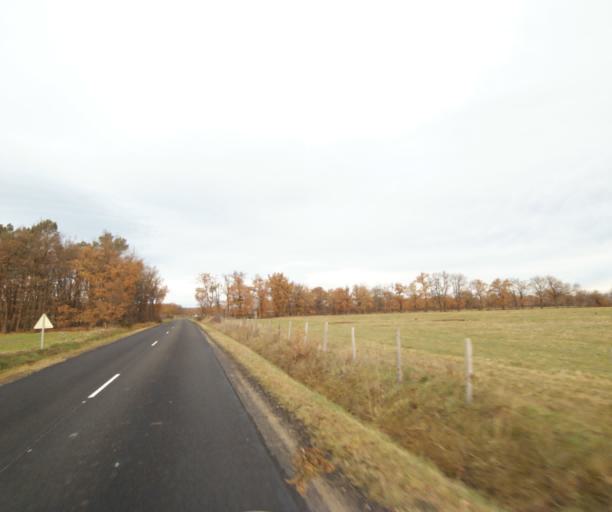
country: FR
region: Rhone-Alpes
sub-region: Departement de la Loire
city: Sury-le-Comtal
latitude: 45.5291
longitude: 4.1581
